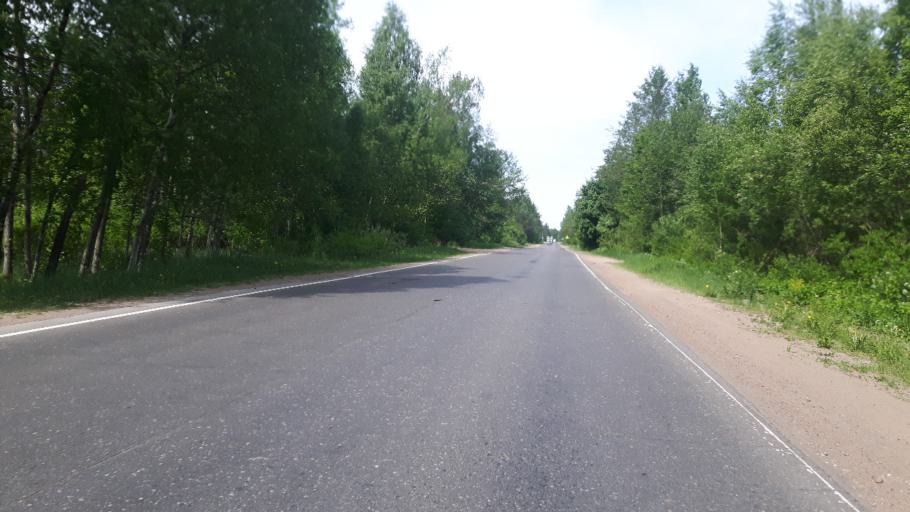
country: RU
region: Leningrad
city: Ust'-Luga
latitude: 59.6422
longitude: 28.2745
